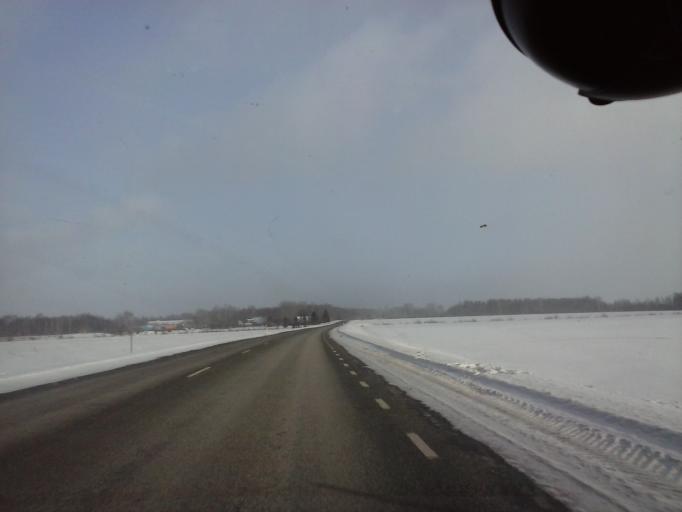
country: EE
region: Tartu
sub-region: Puhja vald
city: Puhja
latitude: 58.3301
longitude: 26.2011
